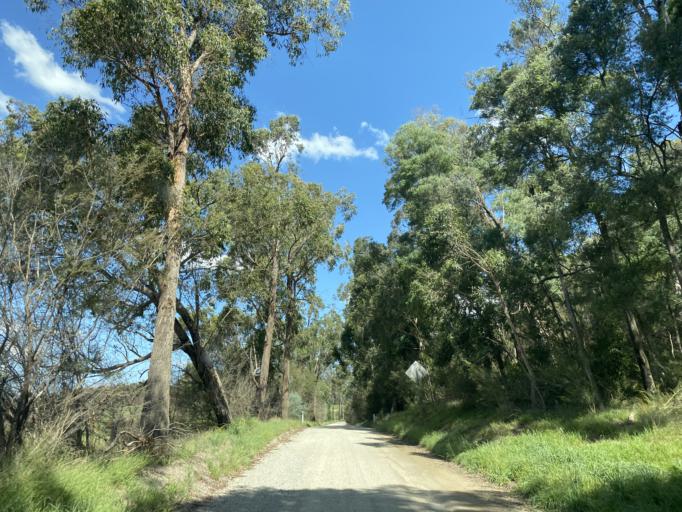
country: AU
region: Victoria
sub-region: Cardinia
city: Bunyip
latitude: -38.0299
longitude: 145.7465
